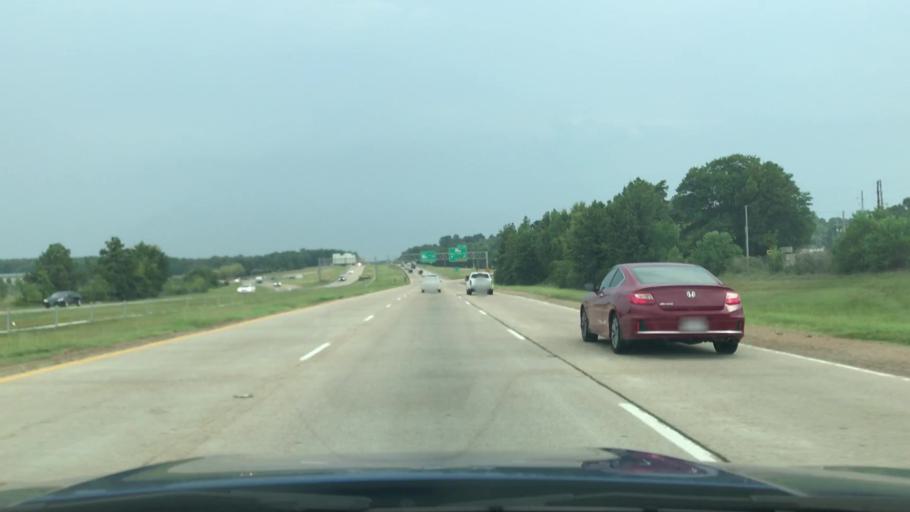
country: US
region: Louisiana
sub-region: Caddo Parish
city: Shreveport
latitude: 32.4474
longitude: -93.8430
